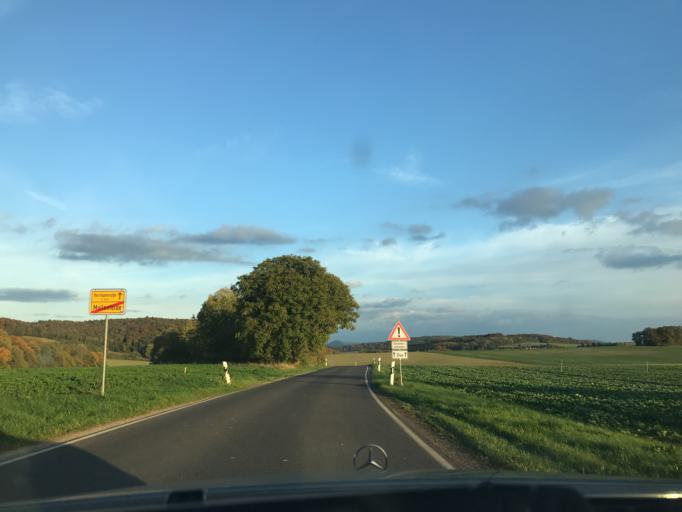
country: DE
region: Hesse
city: Witzenhausen
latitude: 51.4085
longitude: 9.8454
